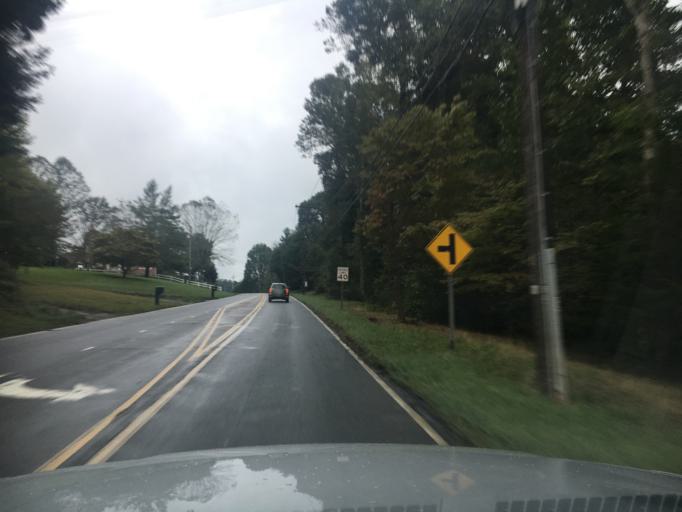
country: US
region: North Carolina
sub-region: Henderson County
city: Laurel Park
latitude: 35.3310
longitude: -82.5192
